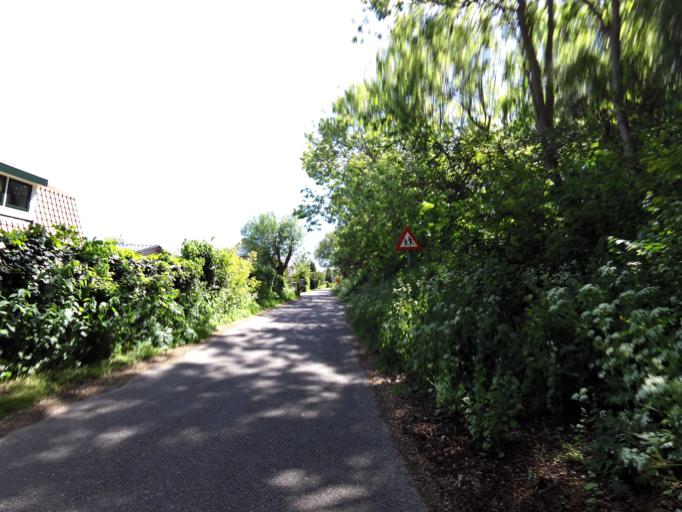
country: NL
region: South Holland
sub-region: Gemeente Hellevoetsluis
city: Nieuw-Helvoet
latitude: 51.8396
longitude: 4.0844
